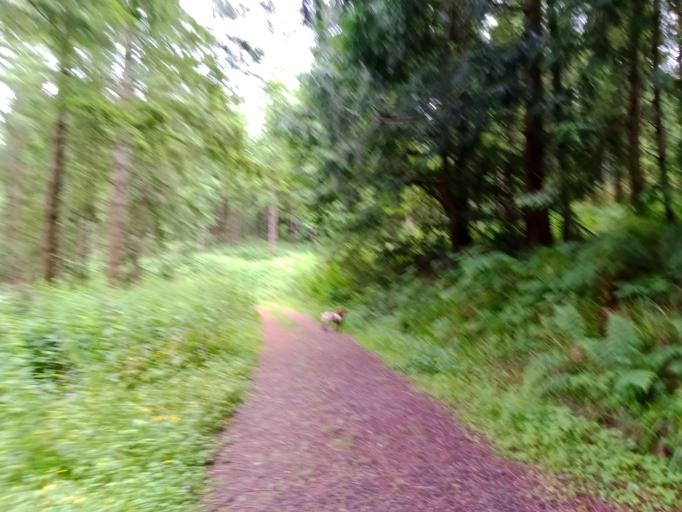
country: IE
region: Leinster
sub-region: Kilkenny
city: Piltown
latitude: 52.4486
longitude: -7.2747
